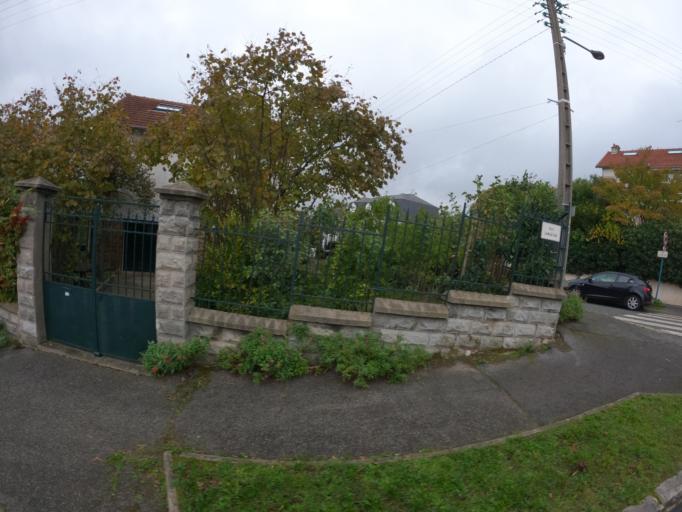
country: FR
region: Ile-de-France
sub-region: Departement du Val-de-Marne
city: Sucy-en-Brie
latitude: 48.7792
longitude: 2.5220
